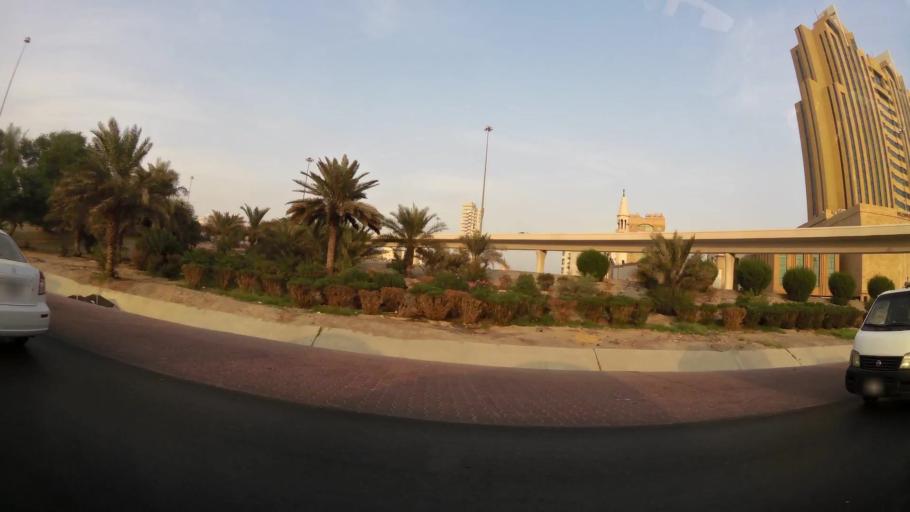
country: KW
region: Muhafazat Hawalli
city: Hawalli
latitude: 29.3301
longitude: 48.0403
